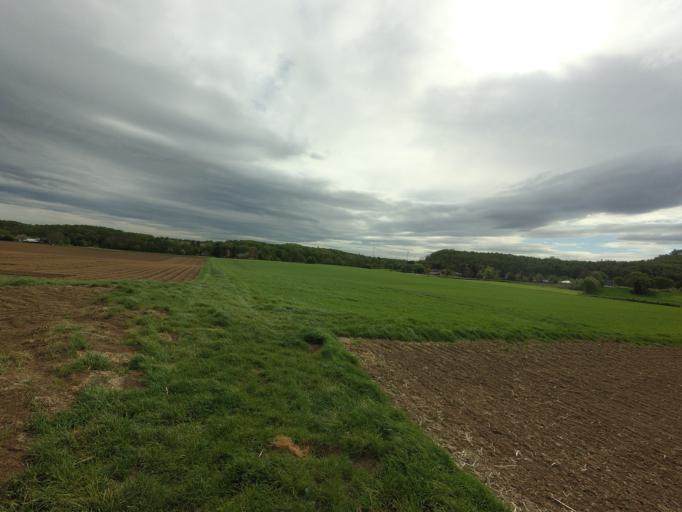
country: DE
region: North Rhine-Westphalia
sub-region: Regierungsbezirk Koln
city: Herzogenrath
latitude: 50.8996
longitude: 6.1043
